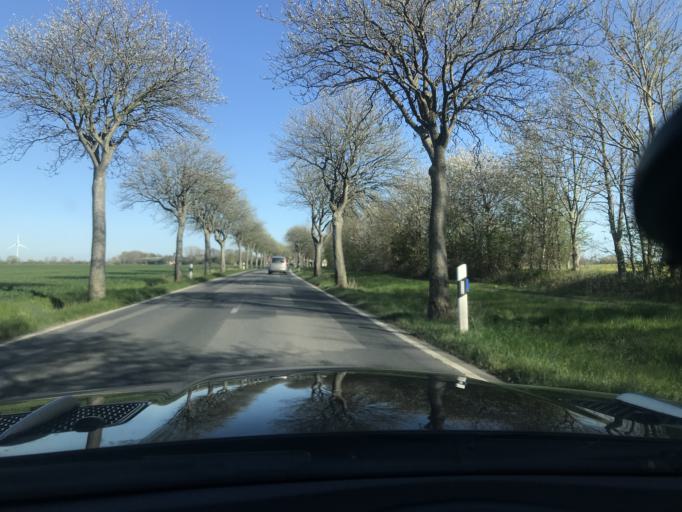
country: DE
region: Schleswig-Holstein
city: Grossenbrode
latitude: 54.4751
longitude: 11.0839
